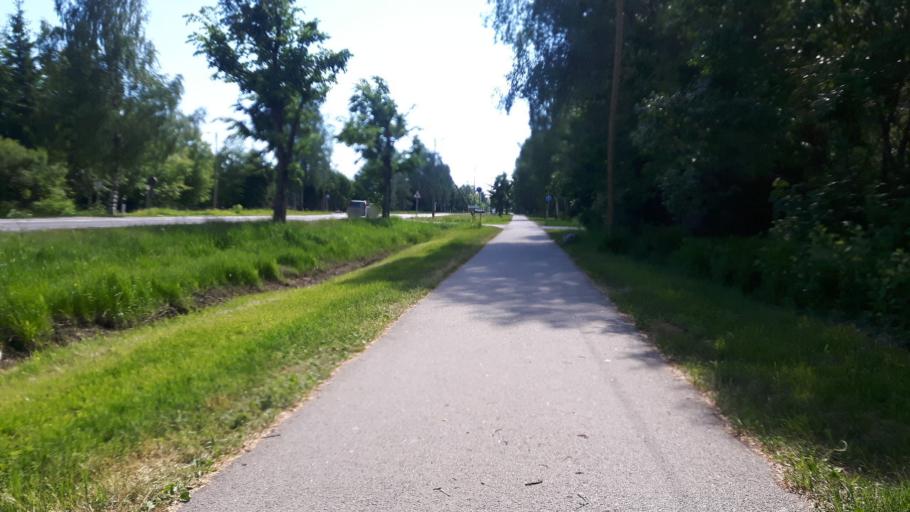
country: EE
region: Paernumaa
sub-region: Paikuse vald
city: Paikuse
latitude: 58.3813
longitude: 24.6319
